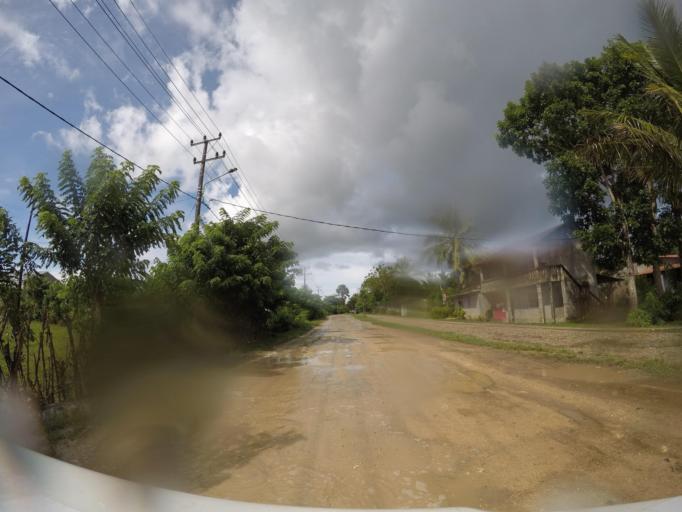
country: TL
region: Lautem
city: Lospalos
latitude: -8.5047
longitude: 127.0070
